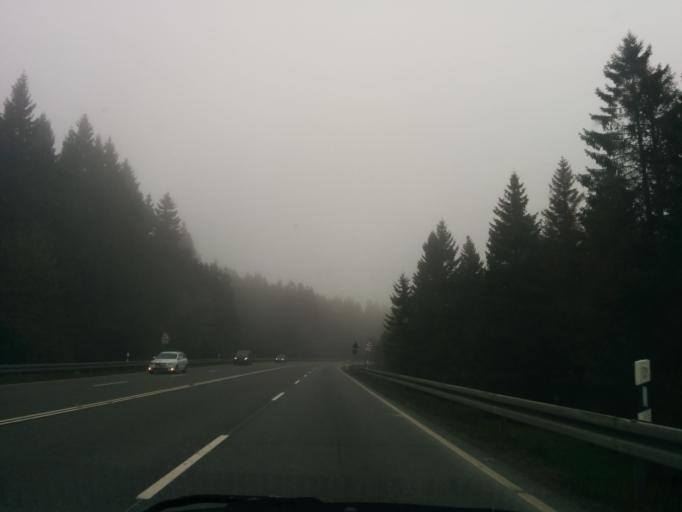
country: DE
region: Lower Saxony
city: Bad Harzburg
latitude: 51.8305
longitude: 10.5235
